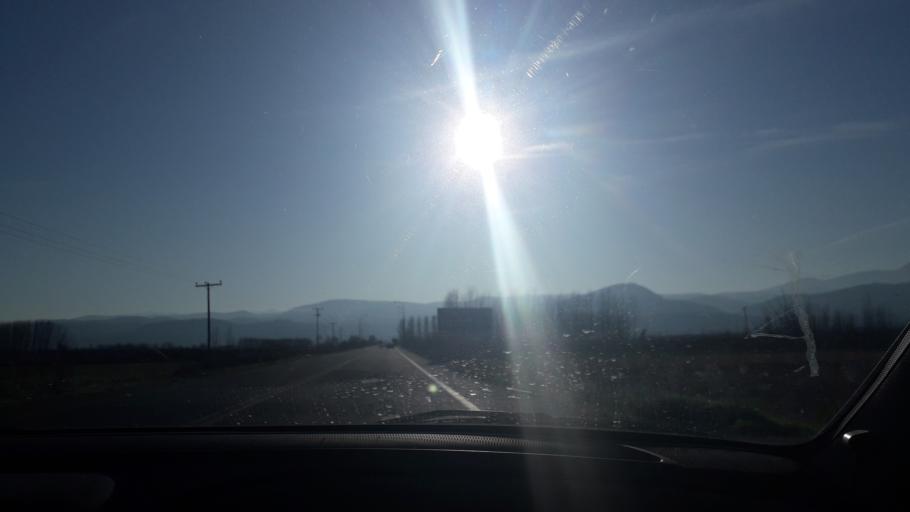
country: GR
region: Central Macedonia
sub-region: Nomos Pellis
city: Apsalos
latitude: 40.9186
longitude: 22.0778
